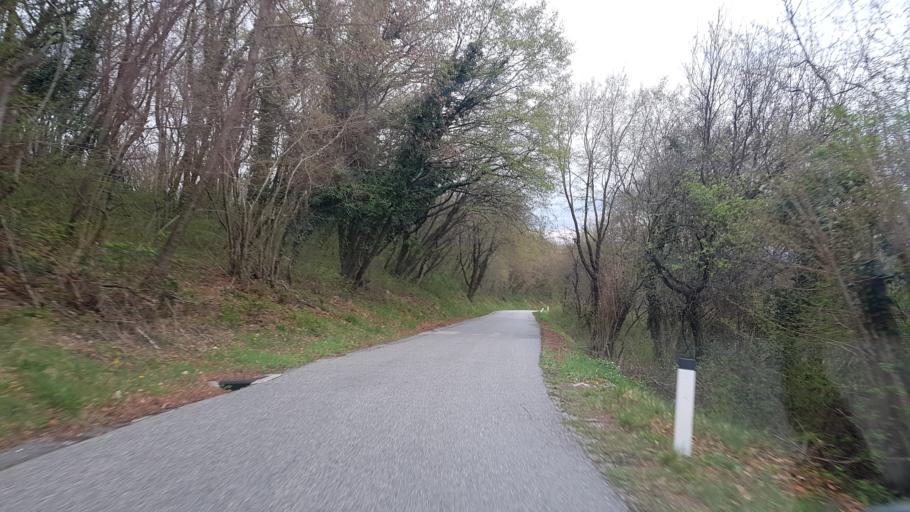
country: SI
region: Kanal
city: Deskle
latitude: 46.0580
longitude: 13.5634
